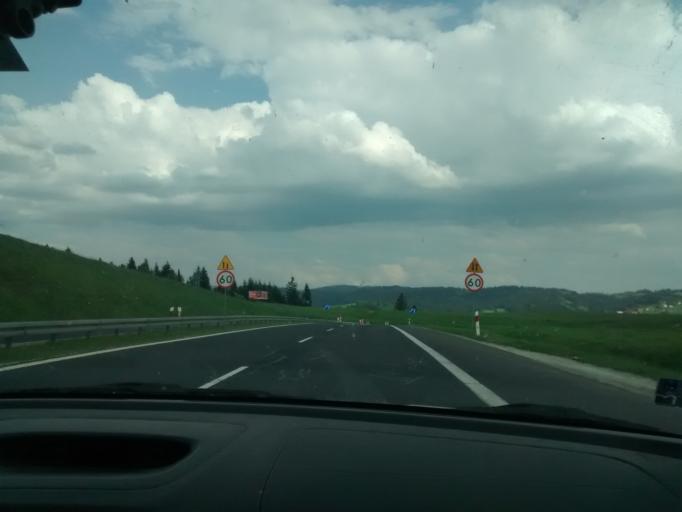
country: PL
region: Lesser Poland Voivodeship
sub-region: Powiat nowotarski
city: Rokiciny
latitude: 49.5743
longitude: 19.9458
